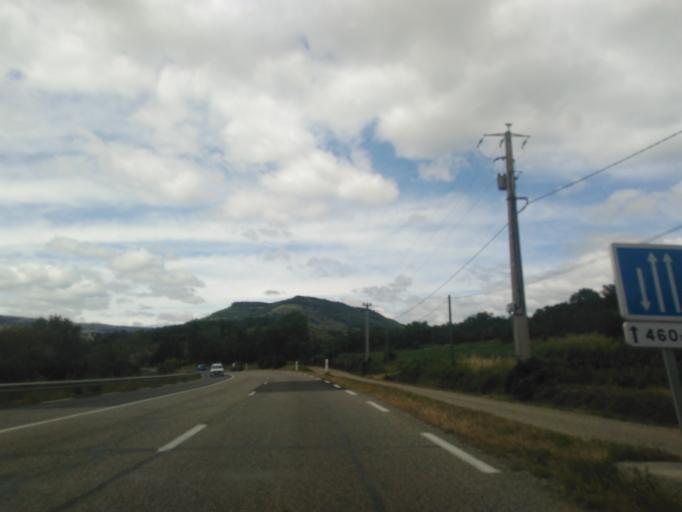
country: FR
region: Rhone-Alpes
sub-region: Departement de l'Ardeche
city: Alba-la-Romaine
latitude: 44.5764
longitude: 4.5783
